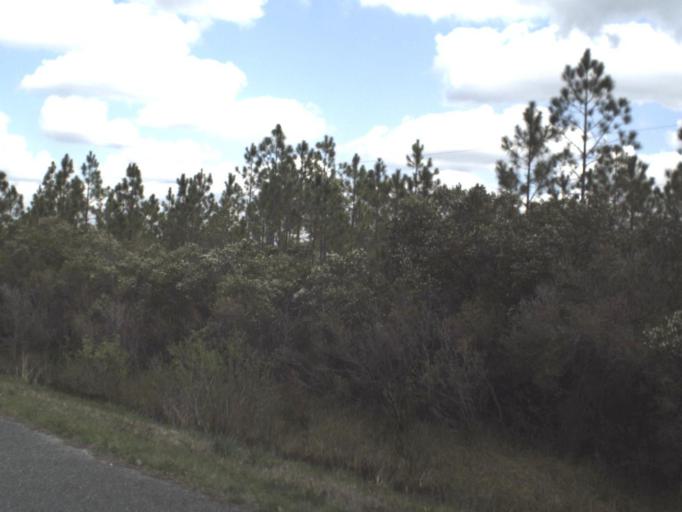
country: US
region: Florida
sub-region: Franklin County
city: Eastpoint
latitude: 29.7964
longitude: -84.8306
